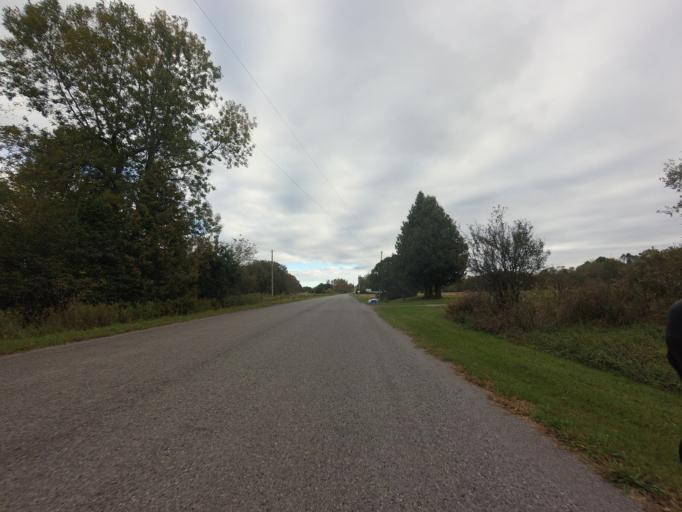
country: CA
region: Ontario
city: Cobourg
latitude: 43.9770
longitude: -78.0650
